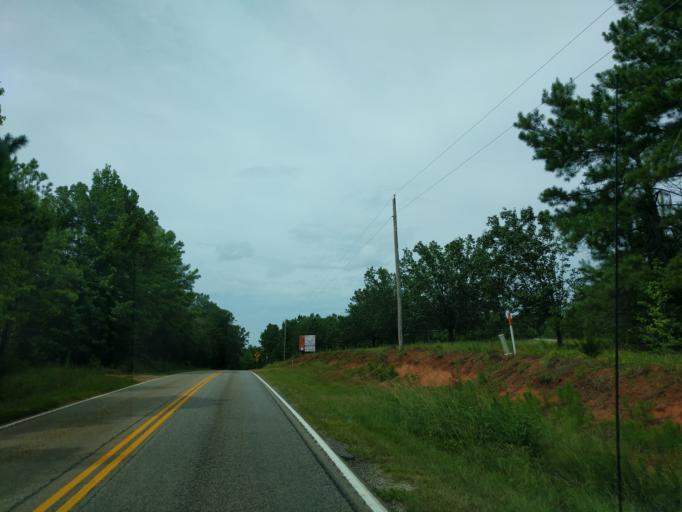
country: US
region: South Carolina
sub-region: Abbeville County
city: Calhoun Falls
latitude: 34.1201
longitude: -82.5963
